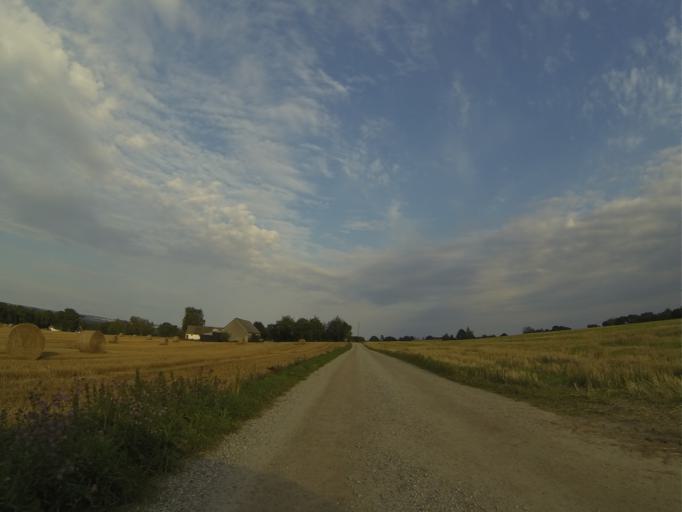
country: SE
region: Skane
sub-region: Lunds Kommun
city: Genarp
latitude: 55.7049
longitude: 13.3647
